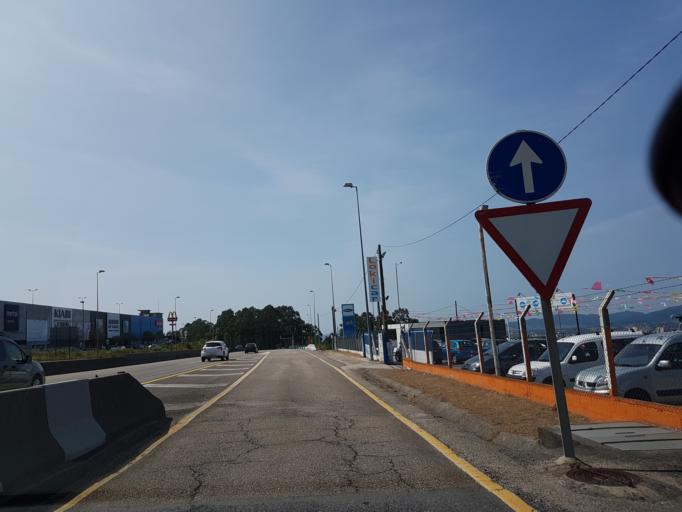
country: ES
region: Galicia
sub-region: Provincia de Pontevedra
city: Vigo
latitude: 42.2173
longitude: -8.6828
